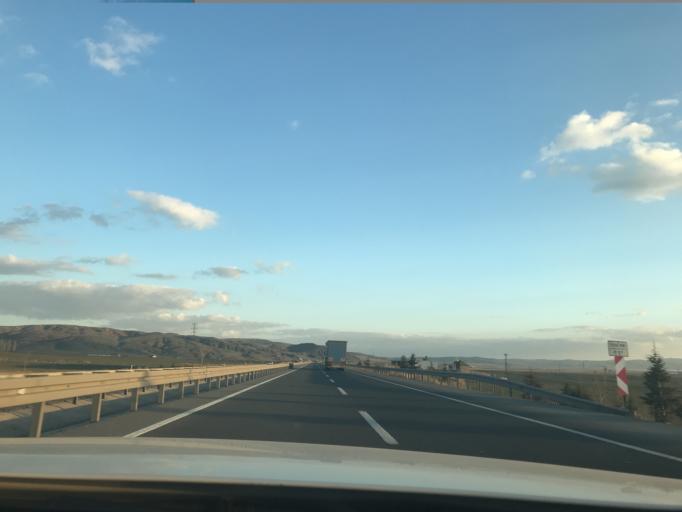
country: TR
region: Ankara
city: Altpinar
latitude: 39.3733
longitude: 32.9002
